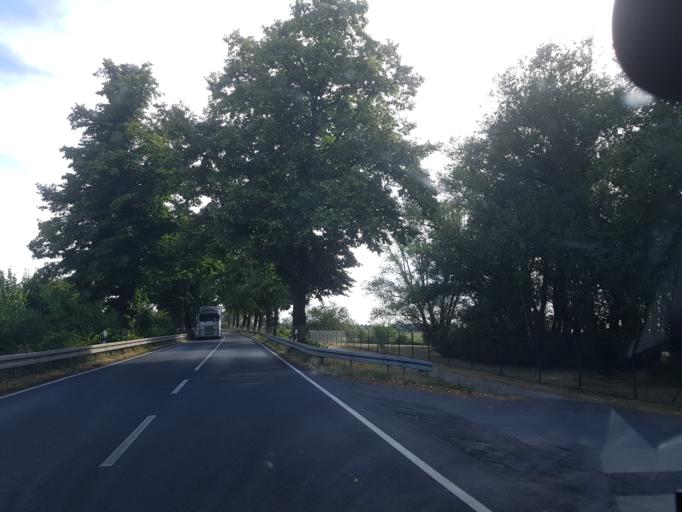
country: DE
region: Brandenburg
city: Herzberg
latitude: 51.7114
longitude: 13.2695
